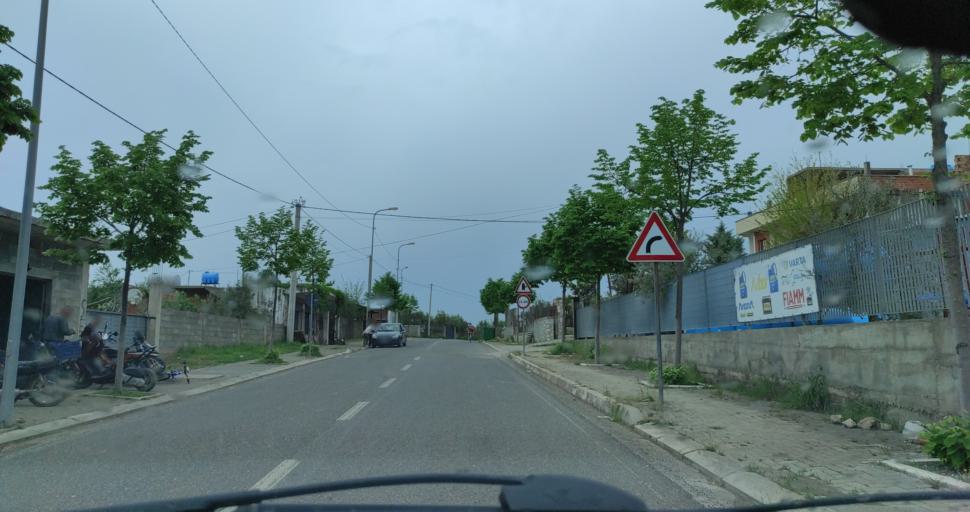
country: AL
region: Lezhe
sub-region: Rrethi i Kurbinit
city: Mamurras
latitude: 41.5865
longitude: 19.6929
